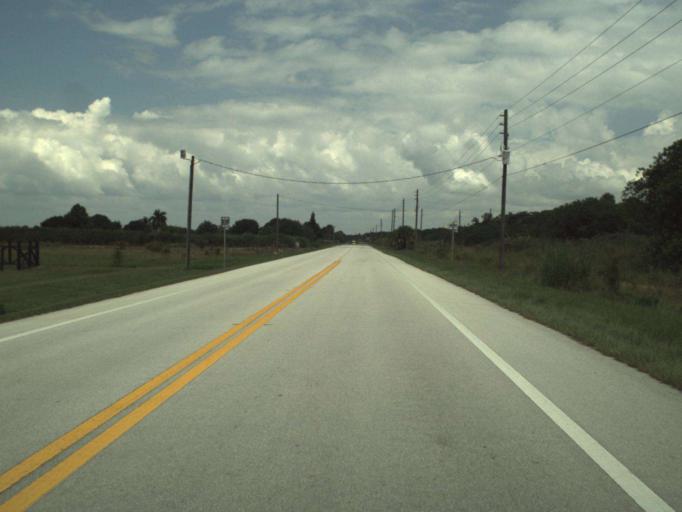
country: US
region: Florida
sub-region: Okeechobee County
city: Taylor Creek
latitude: 27.1125
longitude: -80.6654
